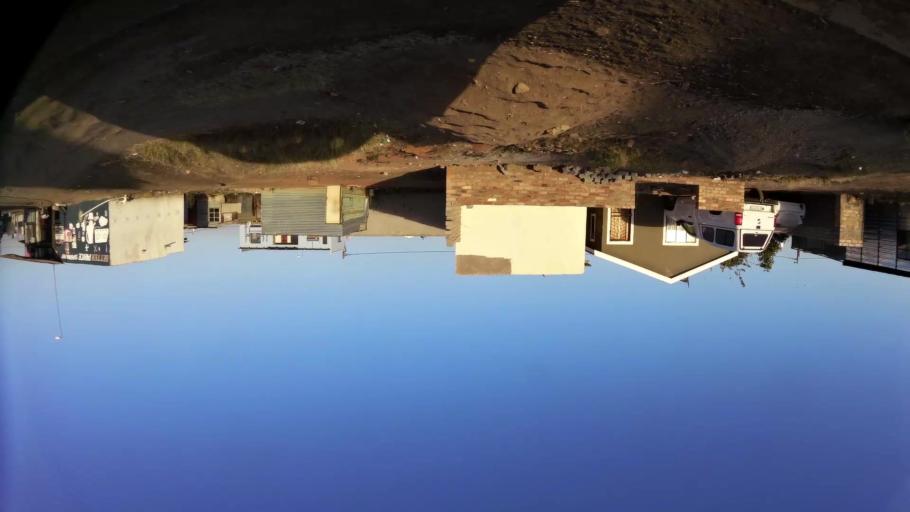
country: ZA
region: North-West
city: Ga-Rankuwa
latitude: -25.5998
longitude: 28.0920
